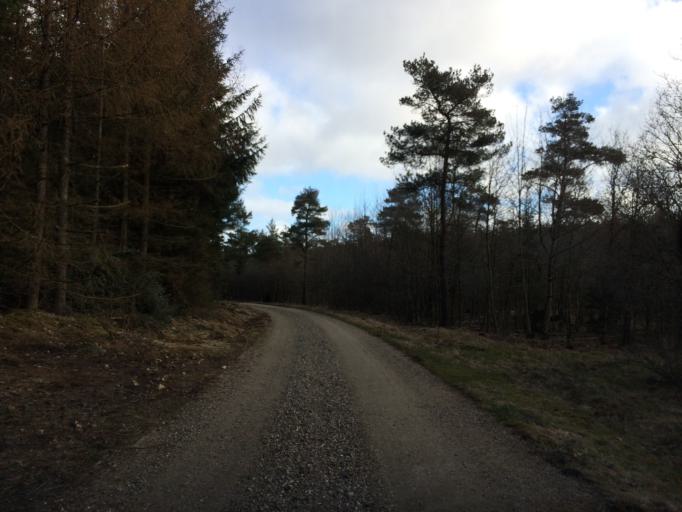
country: DK
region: Central Jutland
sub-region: Holstebro Kommune
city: Ulfborg
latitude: 56.2664
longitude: 8.4469
